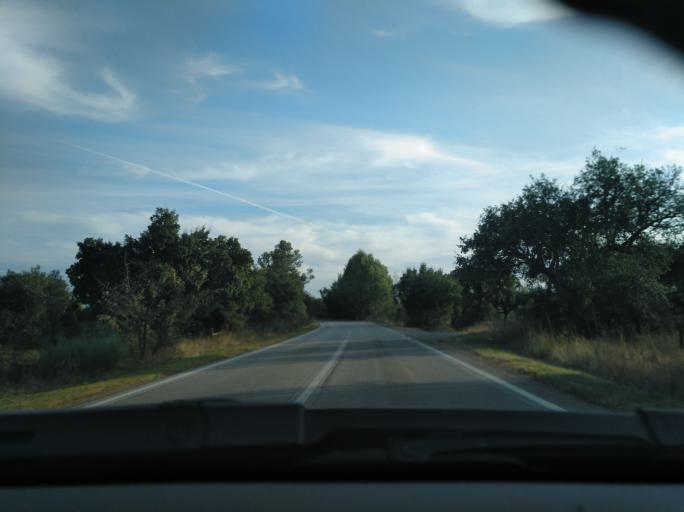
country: PT
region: Portalegre
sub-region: Avis
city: Avis
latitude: 38.9183
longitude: -7.8137
